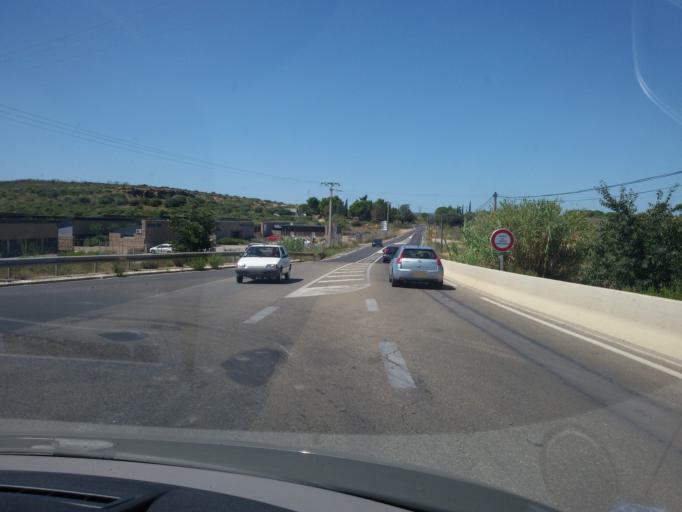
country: FR
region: Languedoc-Roussillon
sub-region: Departement de l'Herault
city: Saint-Jean-de-Vedas
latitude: 43.5454
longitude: 3.8214
